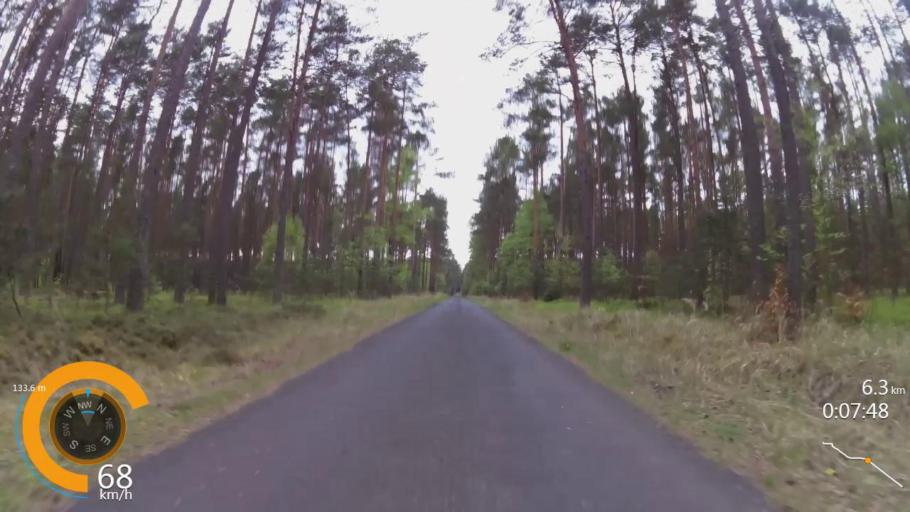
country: PL
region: West Pomeranian Voivodeship
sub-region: Powiat drawski
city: Wierzchowo
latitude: 53.4998
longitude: 16.1581
